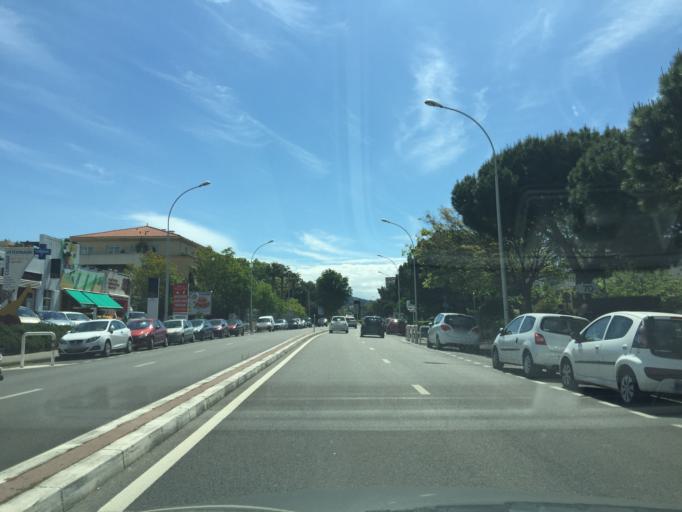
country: FR
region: Provence-Alpes-Cote d'Azur
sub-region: Departement des Bouches-du-Rhone
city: Marseille 09
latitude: 43.2514
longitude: 5.3876
